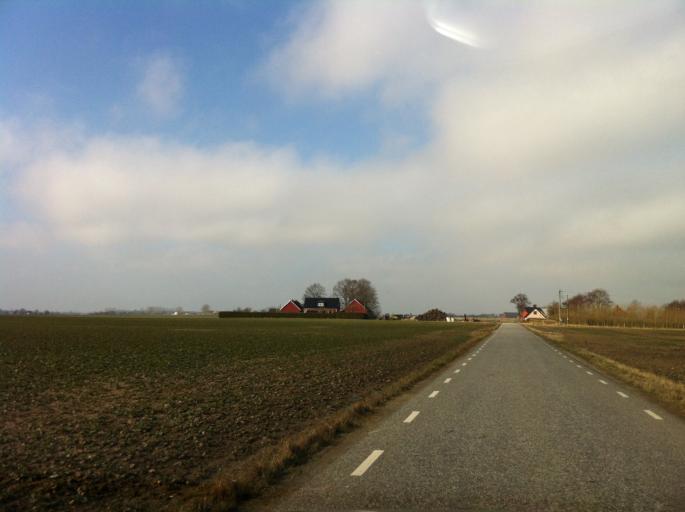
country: SE
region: Skane
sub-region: Svalovs Kommun
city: Teckomatorp
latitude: 55.8618
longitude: 13.0495
